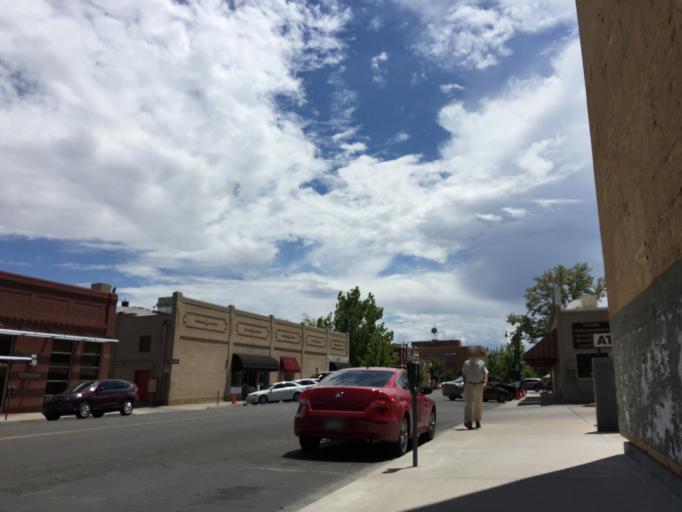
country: US
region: Colorado
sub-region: Mesa County
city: Grand Junction
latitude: 39.0681
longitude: -108.5629
